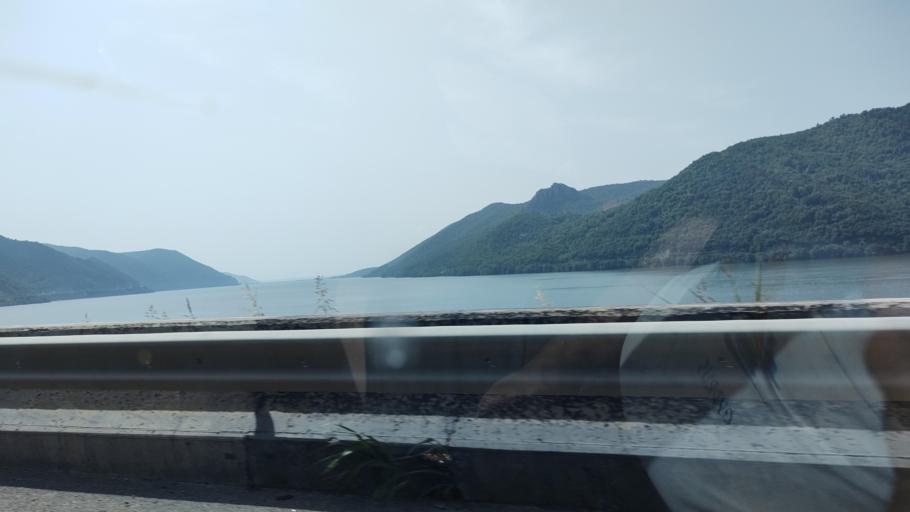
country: RO
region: Mehedinti
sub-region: Comuna Ilovita
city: Ilovita
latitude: 44.7216
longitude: 22.4570
